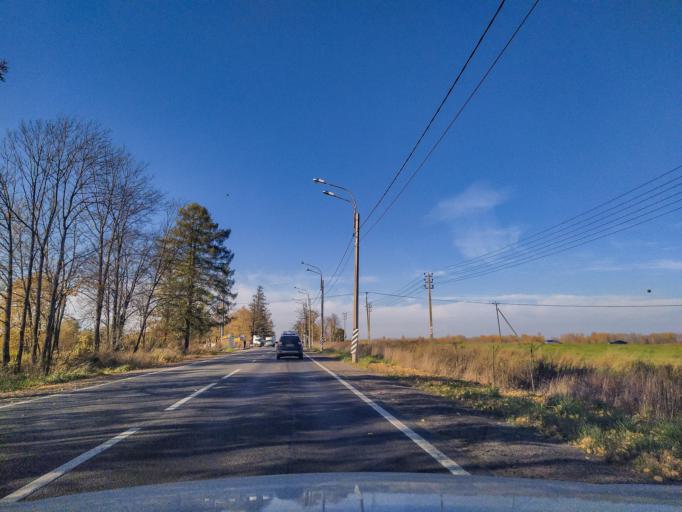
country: RU
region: St.-Petersburg
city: Aleksandrovskaya
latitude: 59.7085
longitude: 30.3270
